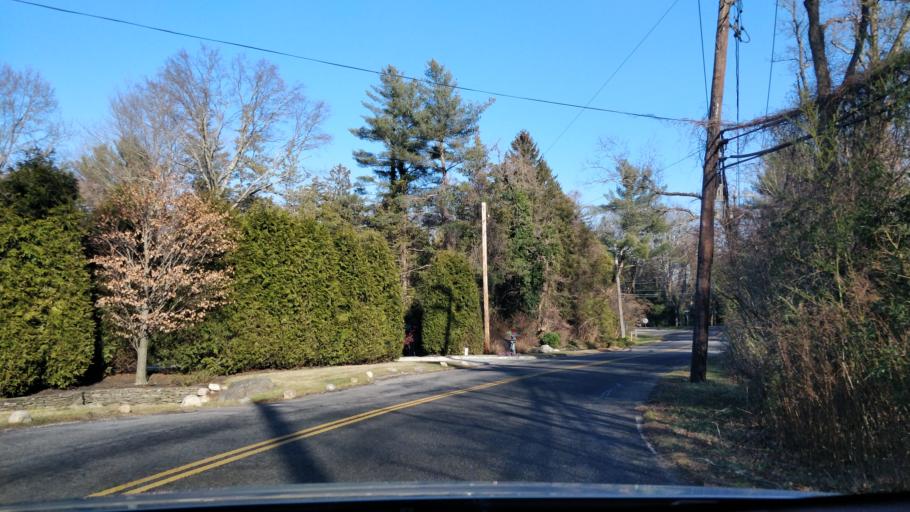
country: US
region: New York
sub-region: Nassau County
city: Glen Head
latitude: 40.8269
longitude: -73.6162
